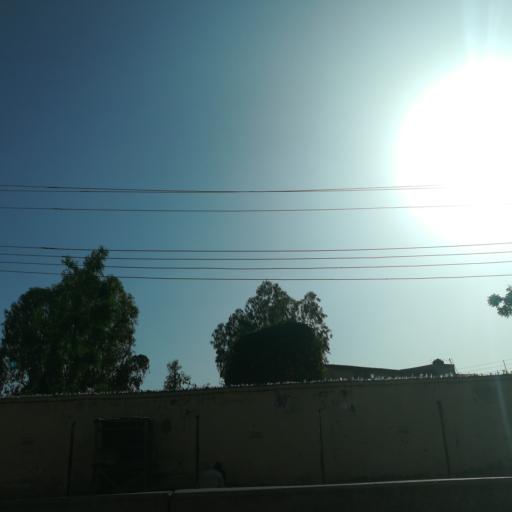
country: NG
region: Kano
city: Kano
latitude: 12.0149
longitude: 8.4977
